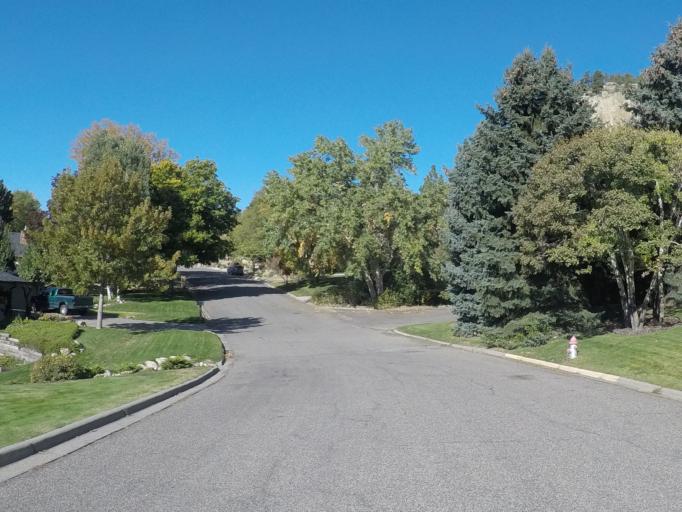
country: US
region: Montana
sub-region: Yellowstone County
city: Billings
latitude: 45.8018
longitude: -108.5860
